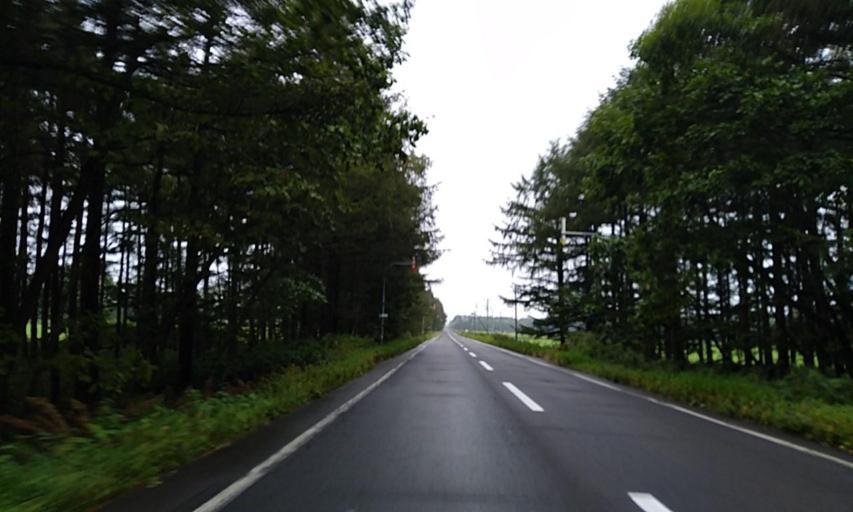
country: JP
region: Hokkaido
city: Shibetsu
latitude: 43.5011
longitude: 144.6560
